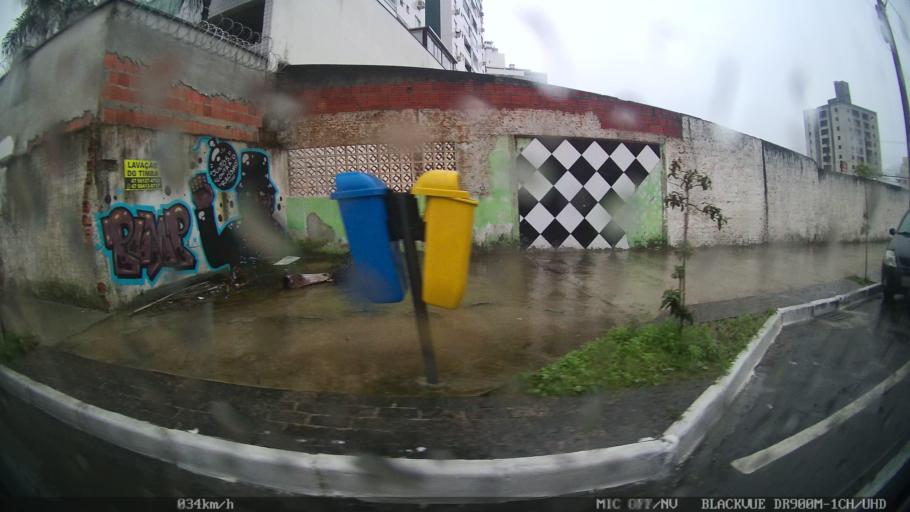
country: BR
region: Santa Catarina
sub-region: Itajai
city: Itajai
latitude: -26.9087
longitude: -48.6811
